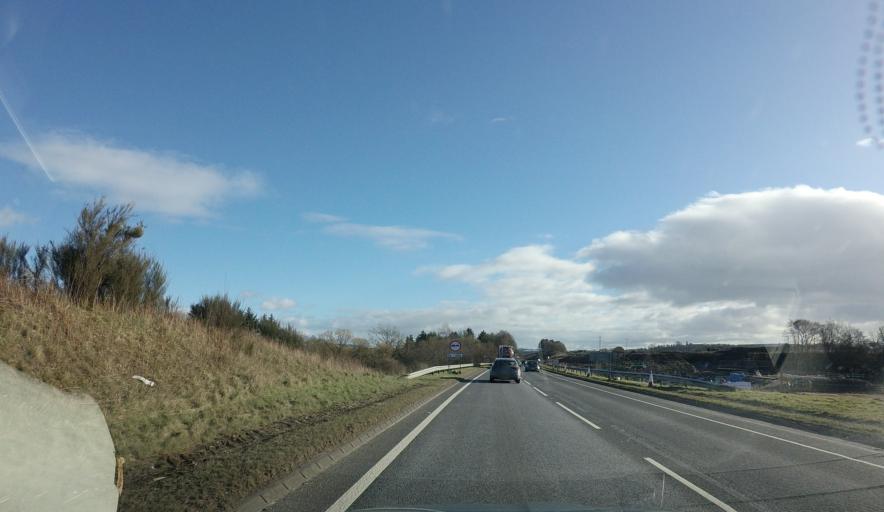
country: GB
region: Scotland
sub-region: Perth and Kinross
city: Luncarty
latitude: 56.4651
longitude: -3.4789
